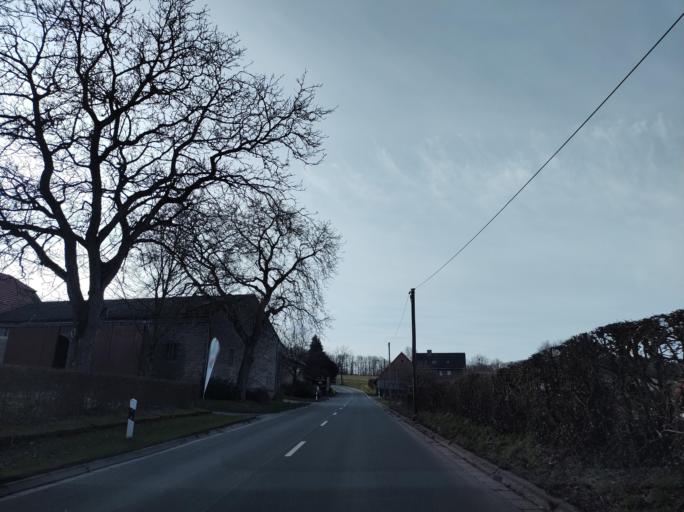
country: DE
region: North Rhine-Westphalia
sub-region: Regierungsbezirk Detmold
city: Horn
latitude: 51.8919
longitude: 8.9019
